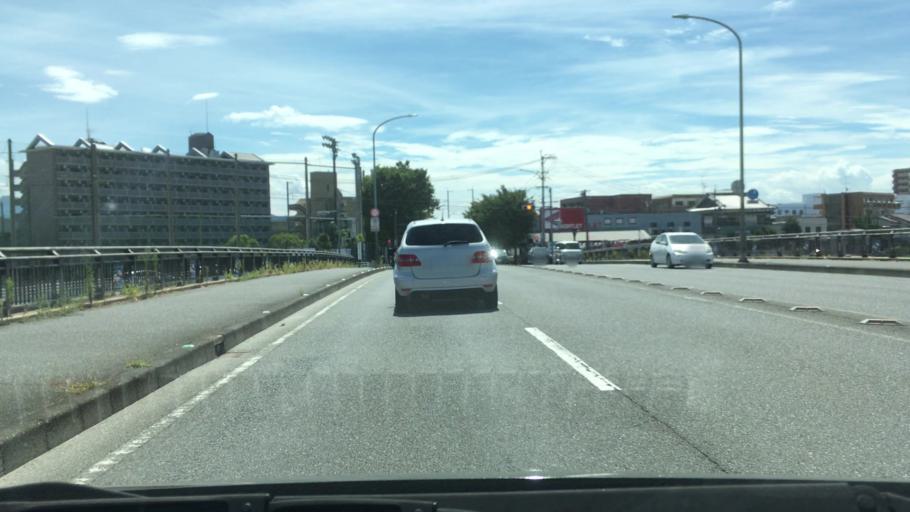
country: JP
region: Fukuoka
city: Fukuoka-shi
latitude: 33.5628
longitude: 130.4331
